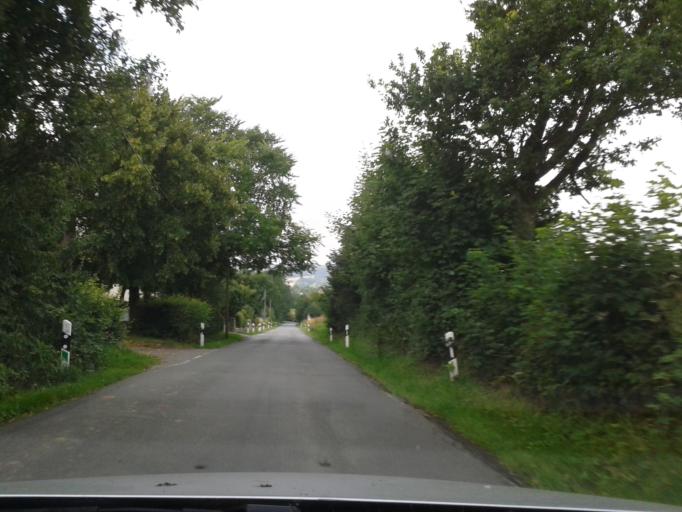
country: DE
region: North Rhine-Westphalia
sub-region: Regierungsbezirk Detmold
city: Dorentrup
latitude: 51.9980
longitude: 8.9952
